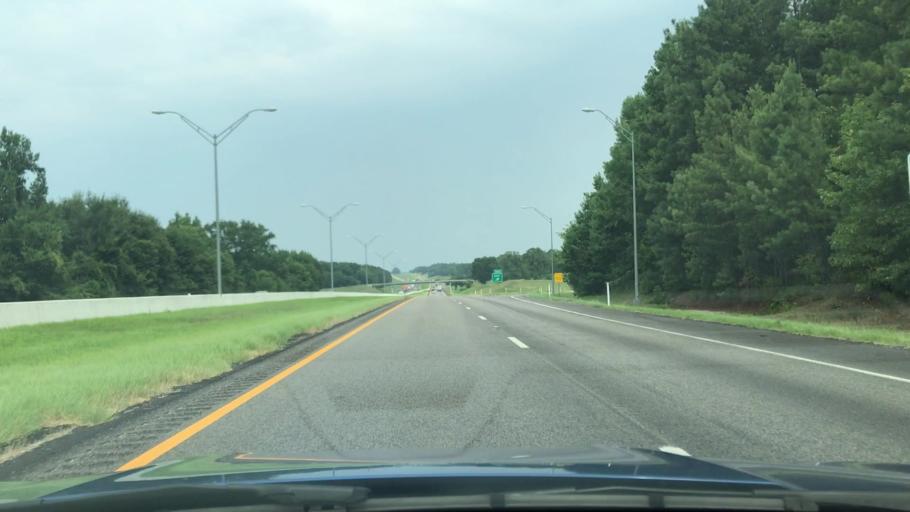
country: US
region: Texas
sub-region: Smith County
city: Tyler
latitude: 32.4522
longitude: -95.2373
